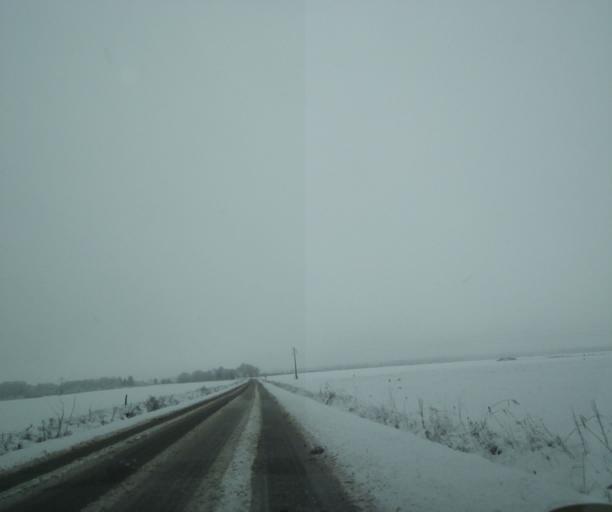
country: FR
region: Champagne-Ardenne
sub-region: Departement de la Haute-Marne
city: Saint-Dizier
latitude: 48.5948
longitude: 4.9053
